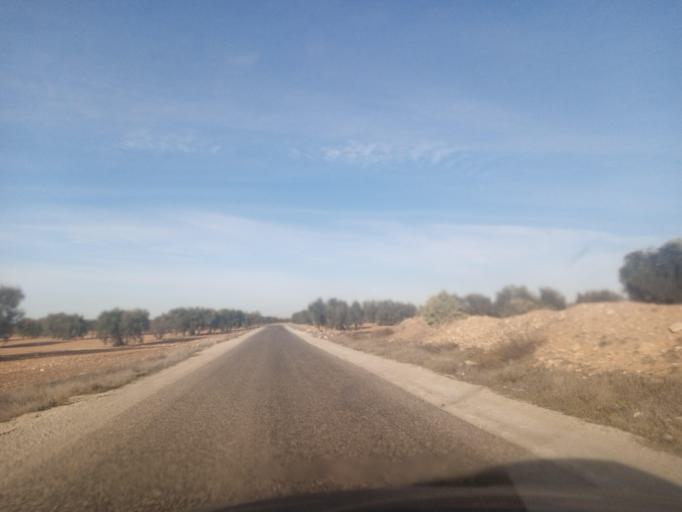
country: TN
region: Safaqis
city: Bi'r `Ali Bin Khalifah
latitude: 34.8883
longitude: 10.1761
